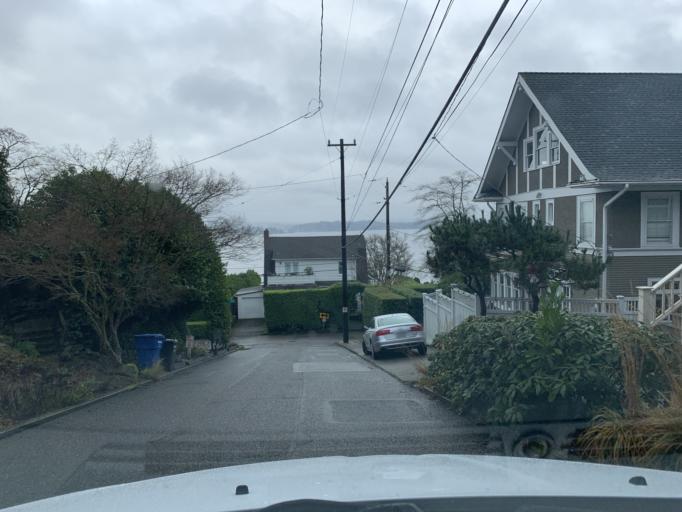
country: US
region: Washington
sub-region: King County
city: Seattle
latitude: 47.6079
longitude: -122.2867
